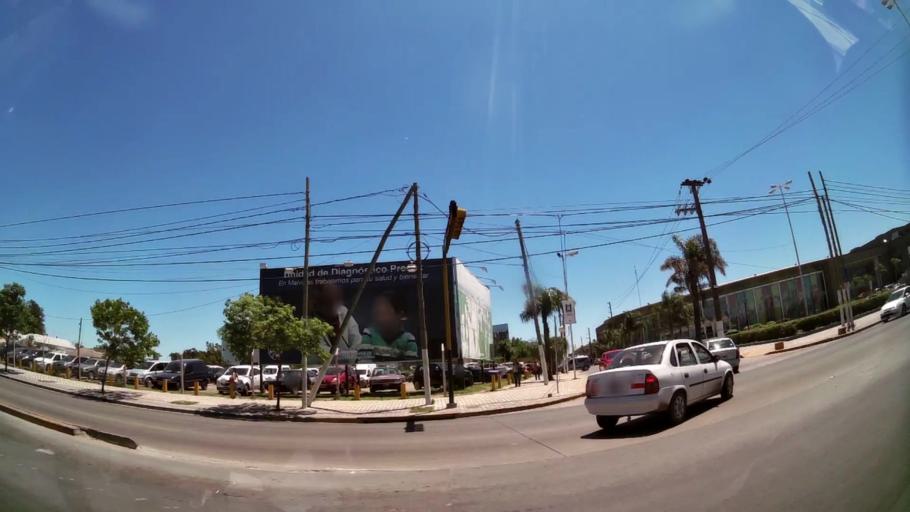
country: AR
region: Buenos Aires
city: Santa Catalina - Dique Lujan
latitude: -34.4972
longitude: -58.7082
